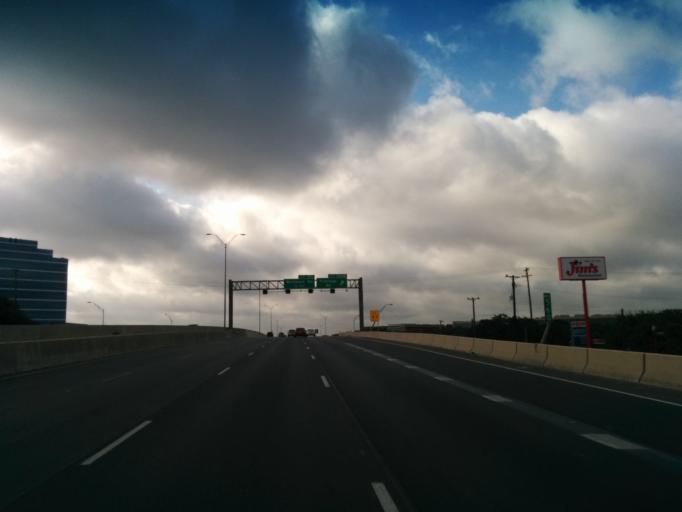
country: US
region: Texas
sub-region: Bexar County
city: Shavano Park
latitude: 29.5455
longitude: -98.5804
